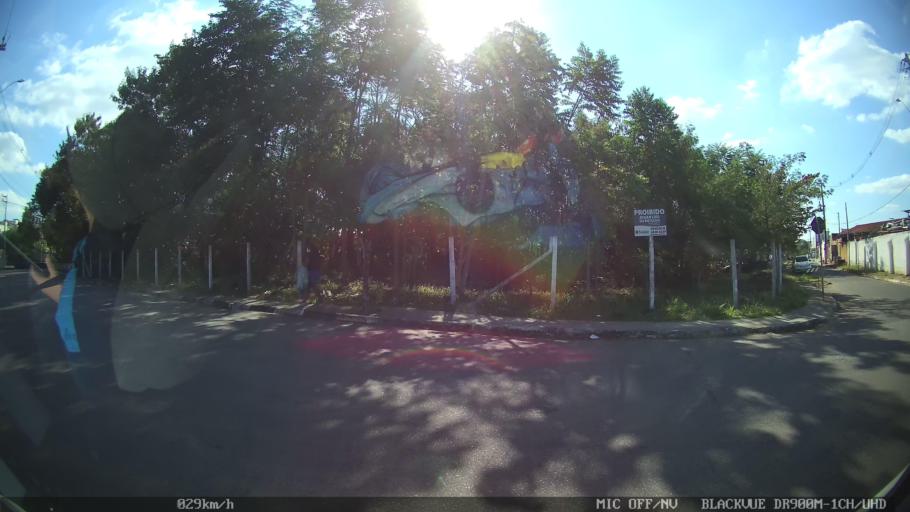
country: BR
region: Sao Paulo
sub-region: Sumare
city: Sumare
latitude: -22.8187
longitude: -47.2794
